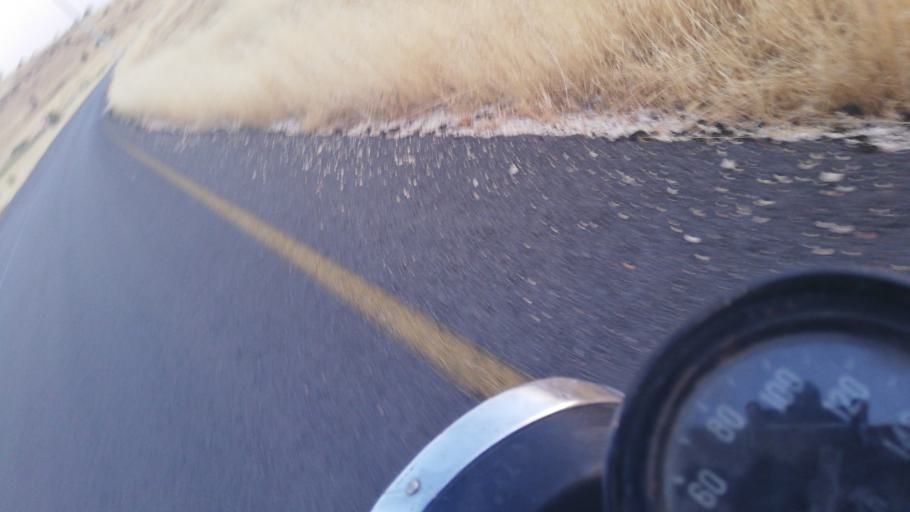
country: TR
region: Mardin
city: Kindirip
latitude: 37.4725
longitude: 41.2280
